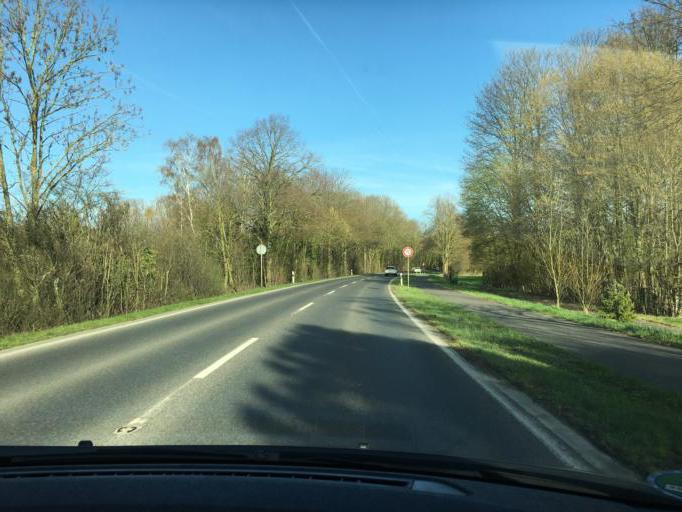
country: DE
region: North Rhine-Westphalia
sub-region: Regierungsbezirk Dusseldorf
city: Korschenbroich
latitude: 51.1948
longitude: 6.5300
